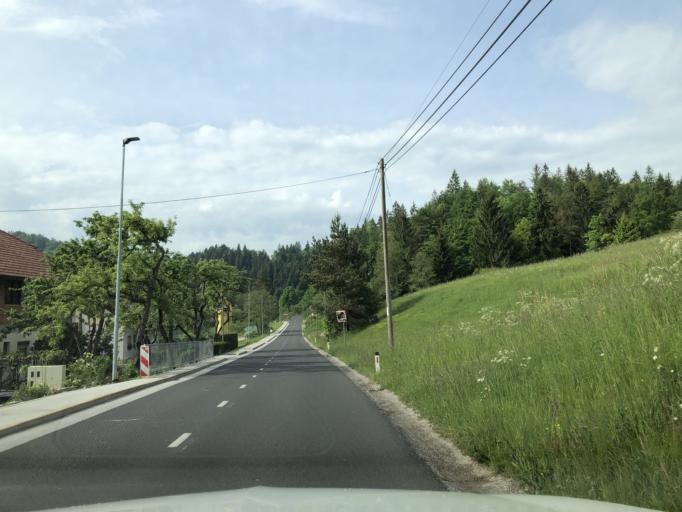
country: SI
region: Velike Lasce
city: Velike Lasce
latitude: 45.8291
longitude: 14.6369
